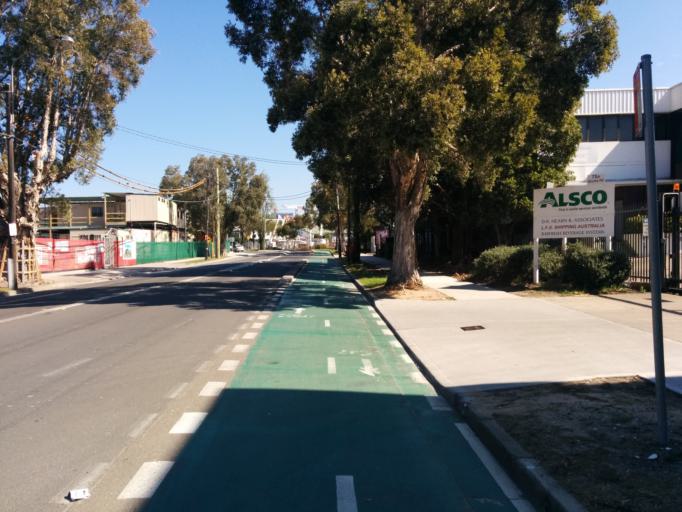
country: AU
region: New South Wales
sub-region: Botany Bay
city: Mascot
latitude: -33.9176
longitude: 151.1888
